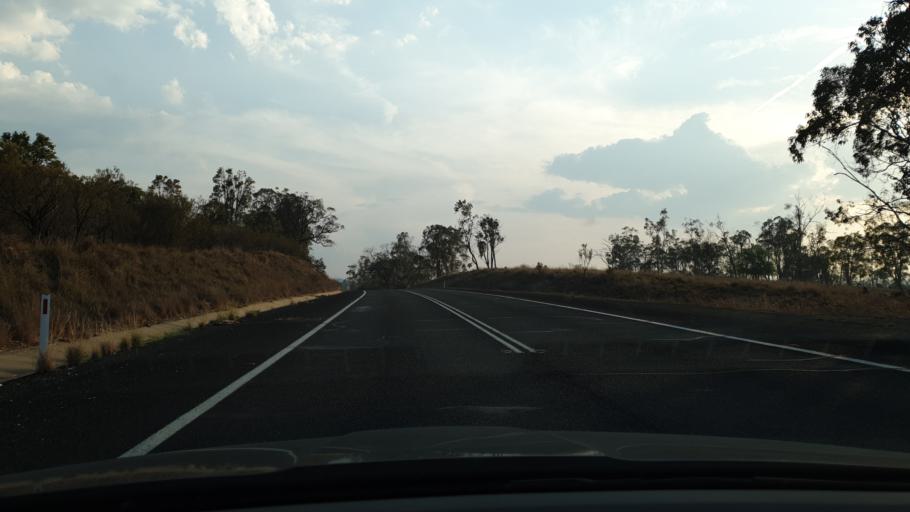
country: AU
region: New South Wales
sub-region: Tenterfield Municipality
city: Carrolls Creek
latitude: -29.2579
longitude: 151.9900
